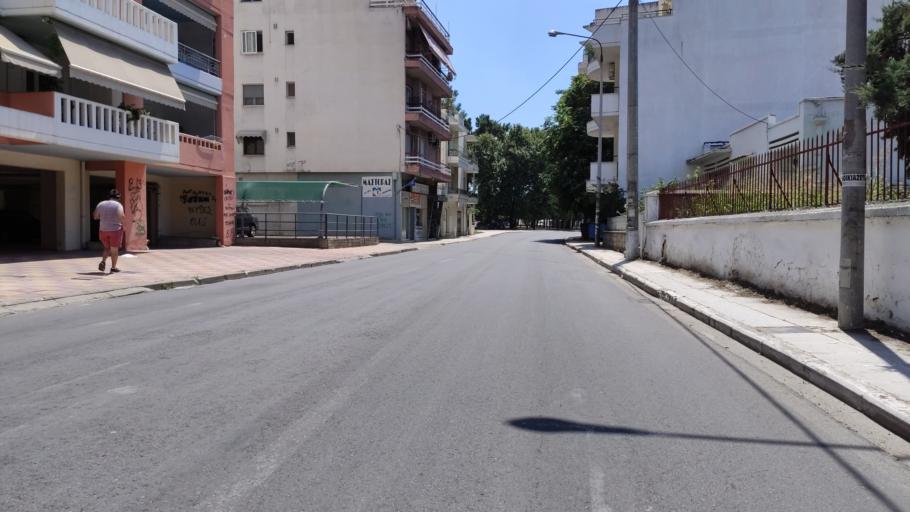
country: GR
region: East Macedonia and Thrace
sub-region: Nomos Rodopis
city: Komotini
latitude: 41.1170
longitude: 25.3978
